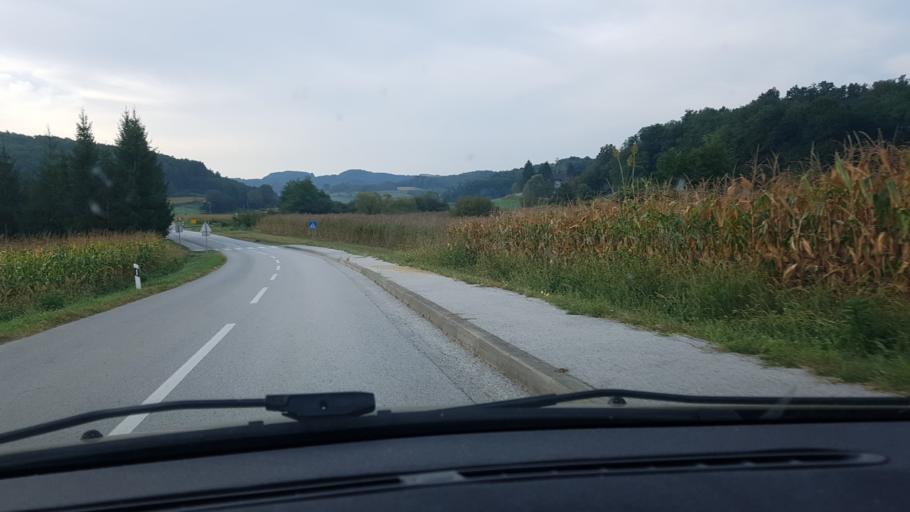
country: HR
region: Krapinsko-Zagorska
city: Mihovljan
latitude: 46.1466
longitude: 15.9616
